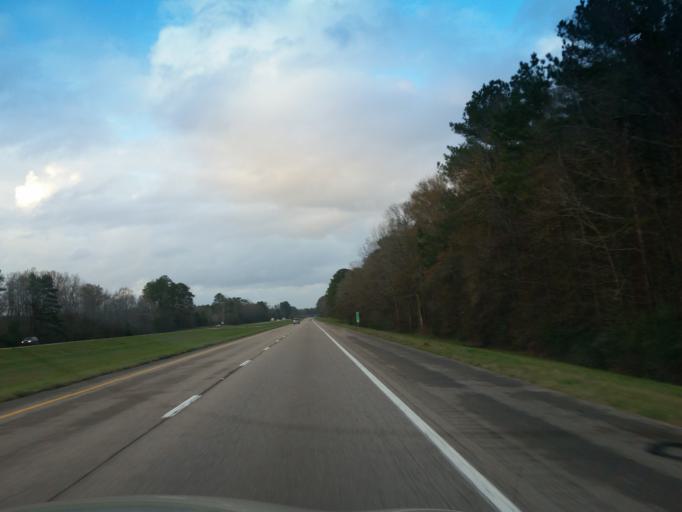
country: US
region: Mississippi
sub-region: Clarke County
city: Stonewall
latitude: 32.0262
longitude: -88.9223
